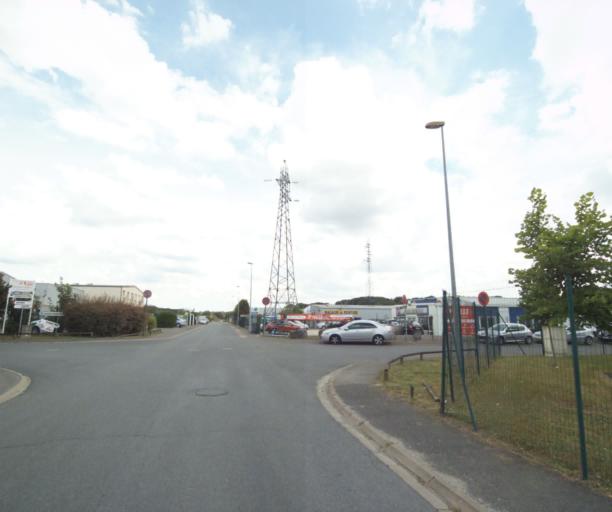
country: FR
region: Ile-de-France
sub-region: Departement de Seine-et-Marne
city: Vulaines-sur-Seine
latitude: 48.4257
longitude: 2.7701
